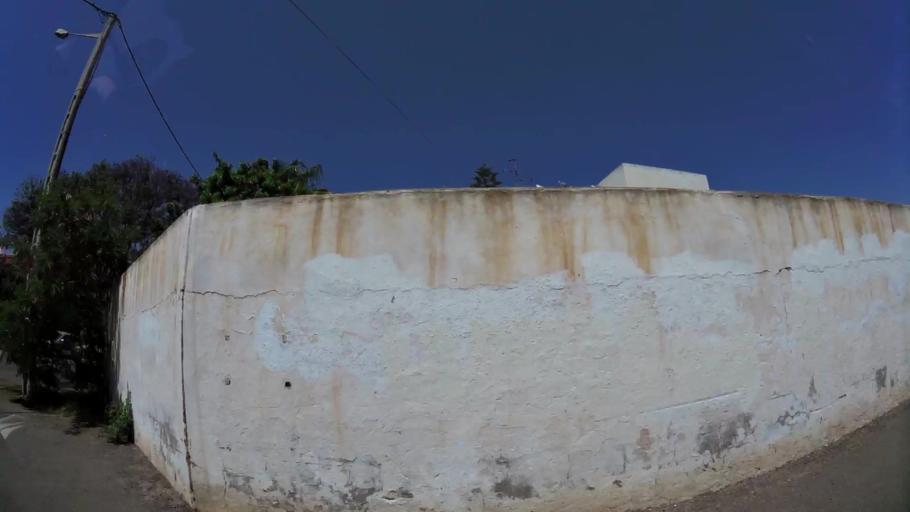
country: MA
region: Souss-Massa-Draa
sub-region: Agadir-Ida-ou-Tnan
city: Agadir
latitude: 30.4296
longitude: -9.5951
